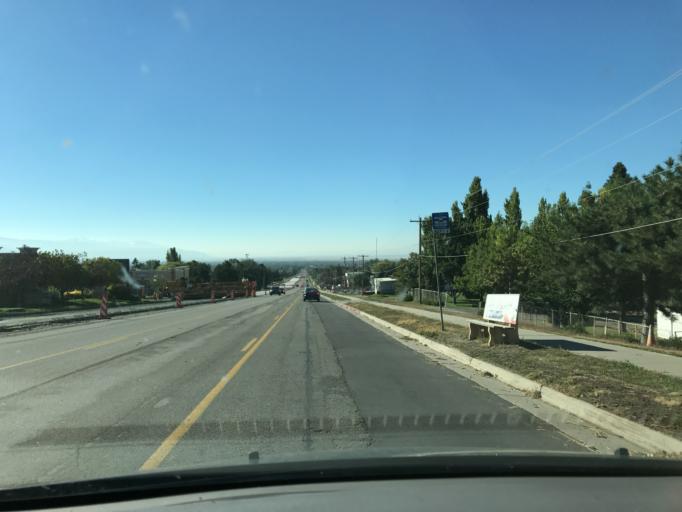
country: US
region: Utah
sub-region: Davis County
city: Hill Air Force Bace
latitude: 41.1002
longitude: -111.9735
